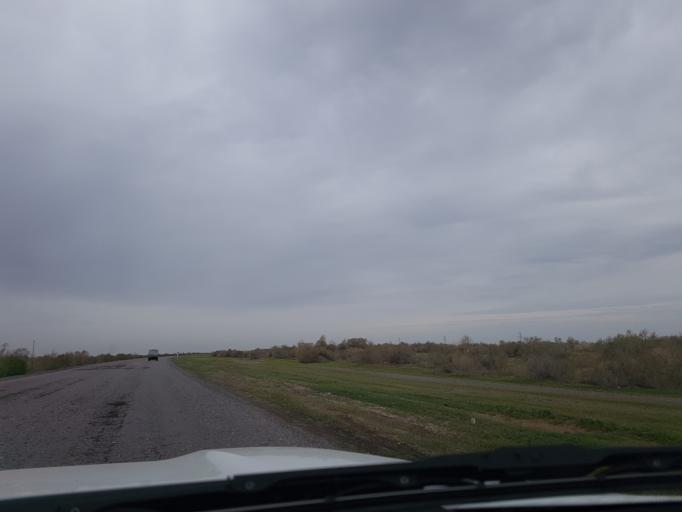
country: TM
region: Lebap
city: Turkmenabat
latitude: 38.8476
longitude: 63.4030
